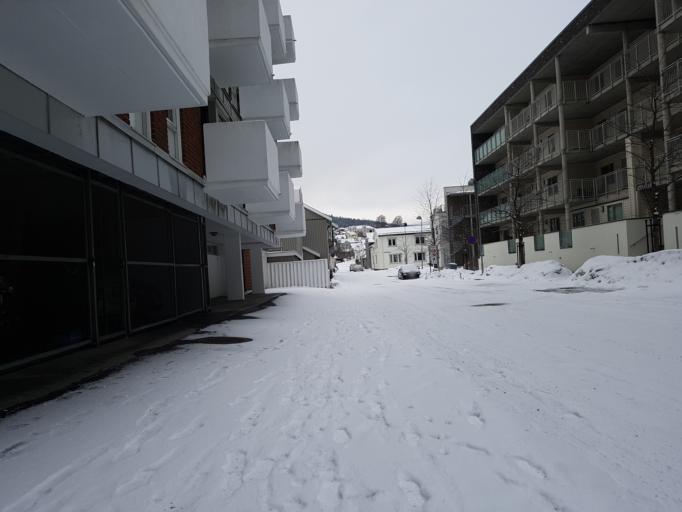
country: NO
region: Buskerud
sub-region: Drammen
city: Drammen
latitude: 59.7378
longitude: 10.1961
